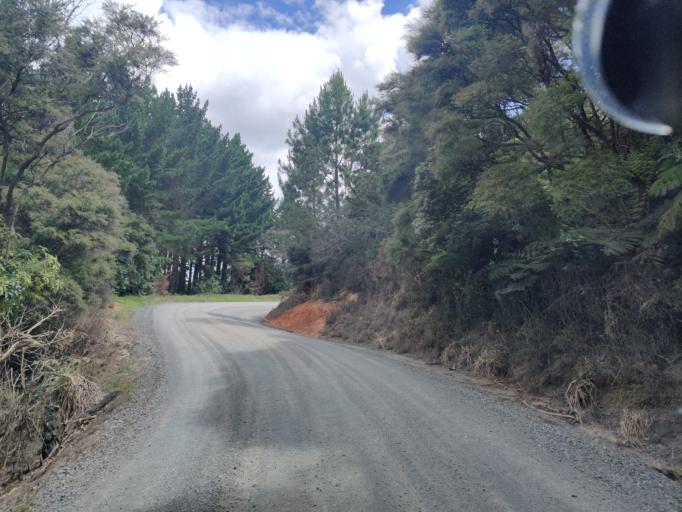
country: NZ
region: Northland
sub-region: Far North District
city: Paihia
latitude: -35.2610
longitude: 174.0495
